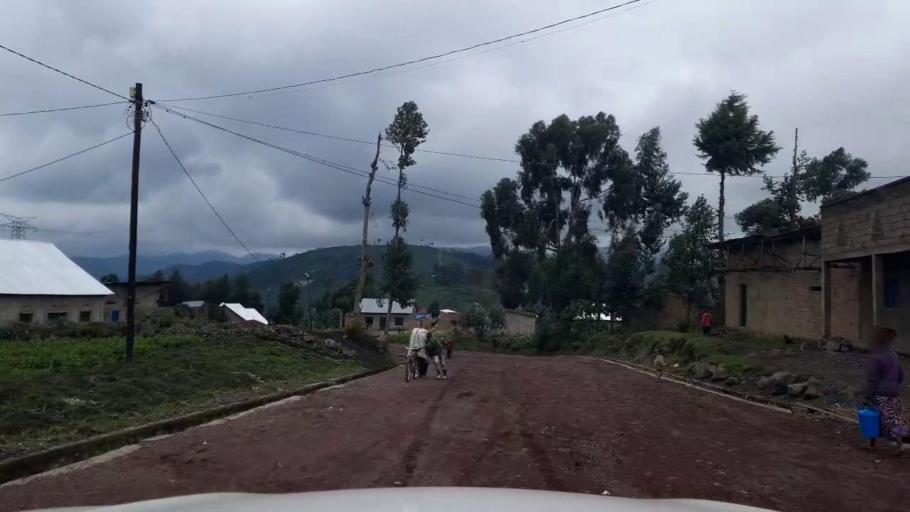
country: RW
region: Northern Province
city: Musanze
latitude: -1.6060
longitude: 29.4512
